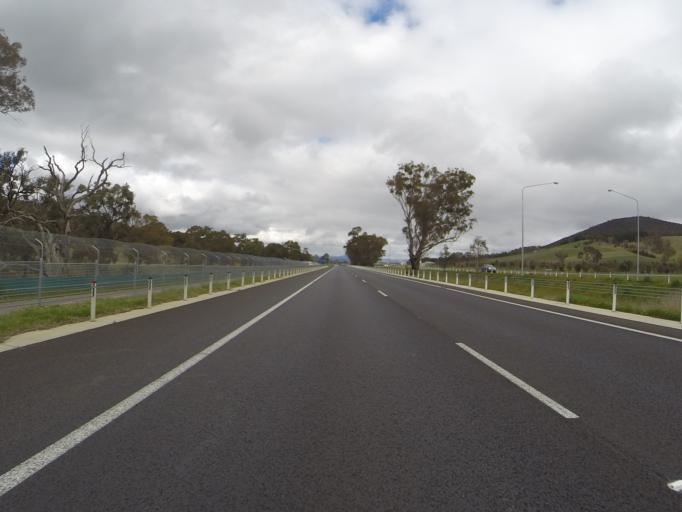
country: AU
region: Australian Capital Territory
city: Canberra
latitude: -35.2233
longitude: 149.1962
